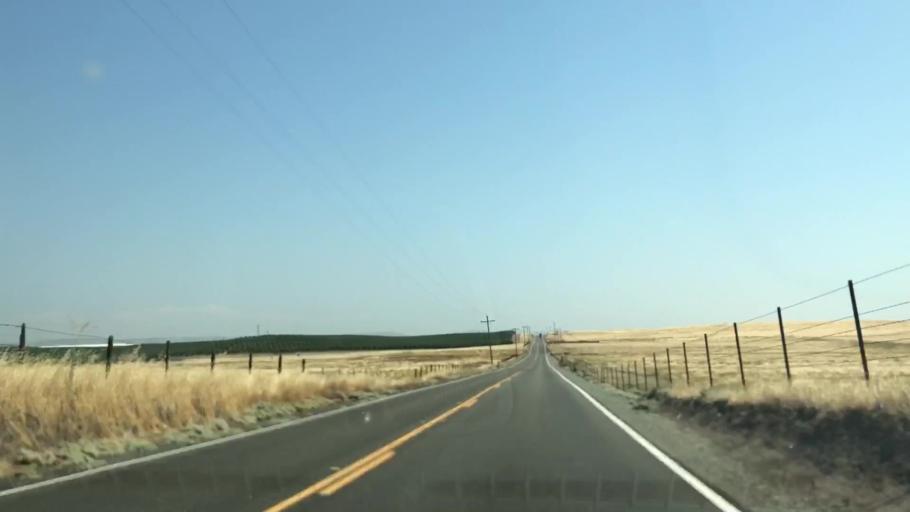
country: US
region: California
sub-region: San Joaquin County
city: Escalon
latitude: 37.9485
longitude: -120.9098
